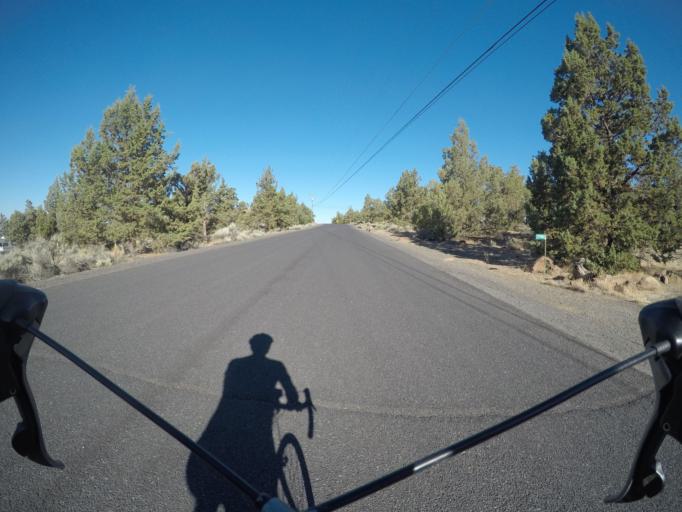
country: US
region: Oregon
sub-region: Deschutes County
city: Bend
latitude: 44.1730
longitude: -121.2740
